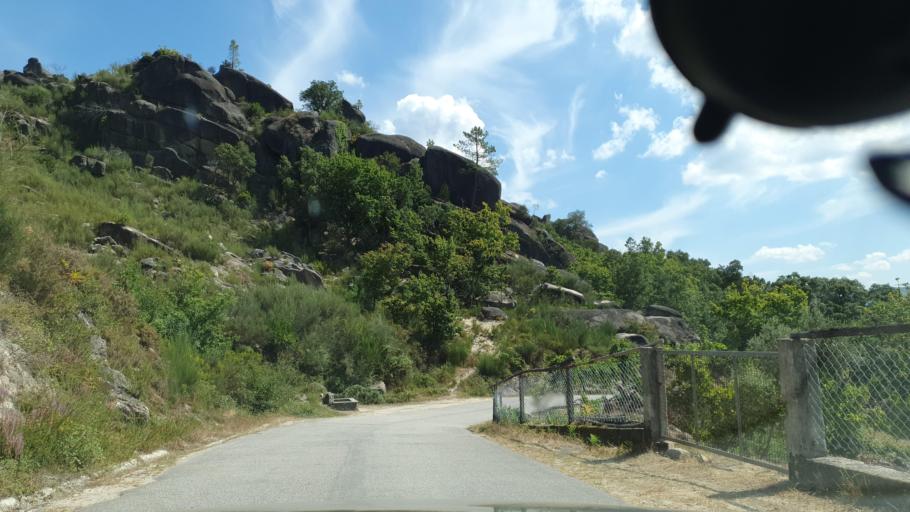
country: PT
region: Braga
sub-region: Vieira do Minho
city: Vieira do Minho
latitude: 41.7050
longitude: -8.0811
